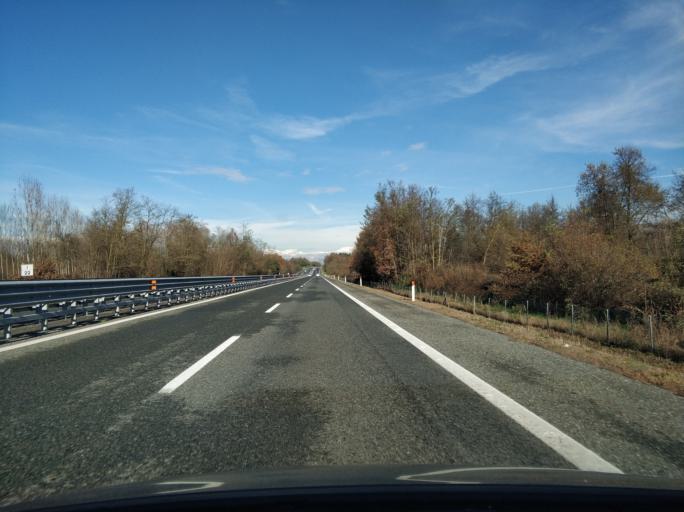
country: IT
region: Piedmont
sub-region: Provincia di Torino
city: Foglizzo
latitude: 45.2930
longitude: 7.8158
